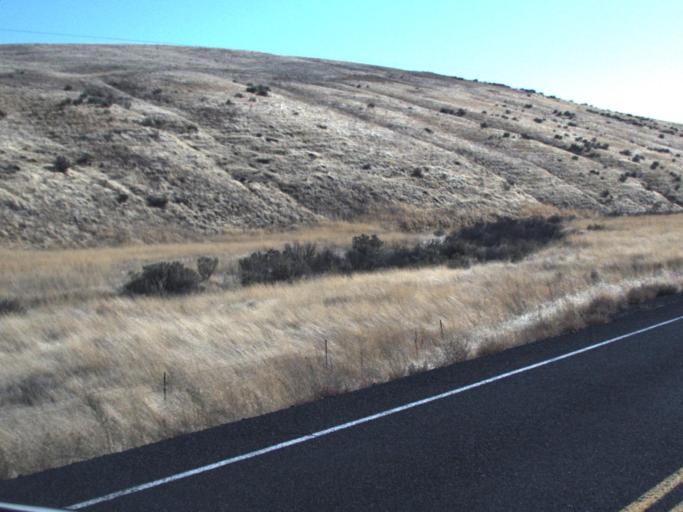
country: US
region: Washington
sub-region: Franklin County
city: Connell
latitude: 46.6713
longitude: -118.5461
